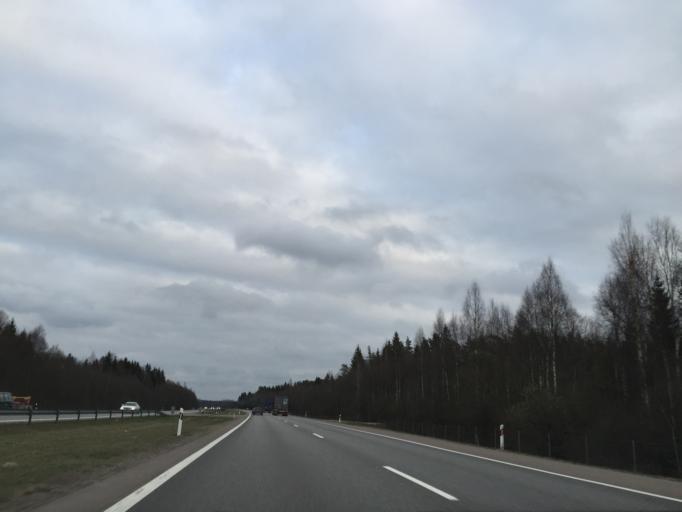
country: LT
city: Rietavas
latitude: 55.6145
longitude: 22.0159
